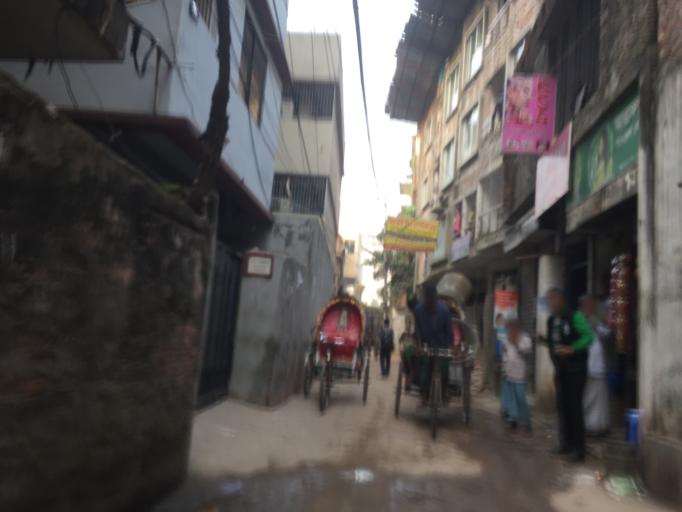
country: BD
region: Dhaka
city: Azimpur
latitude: 23.7534
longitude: 90.3634
